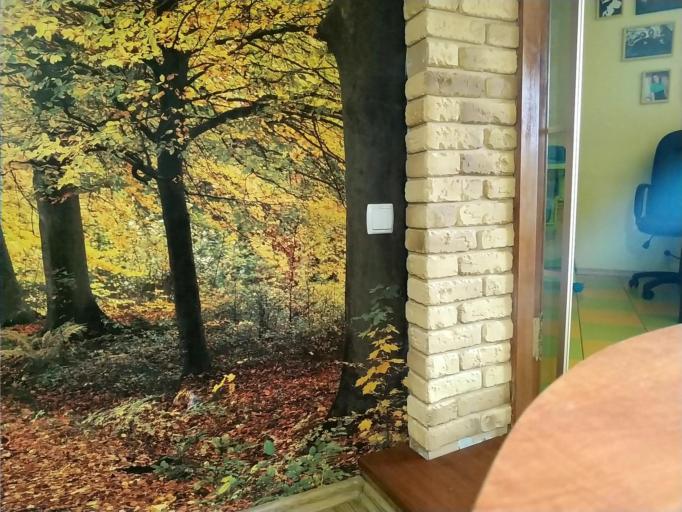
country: BY
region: Mogilev
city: Khotsimsk
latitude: 53.5603
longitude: 32.5309
